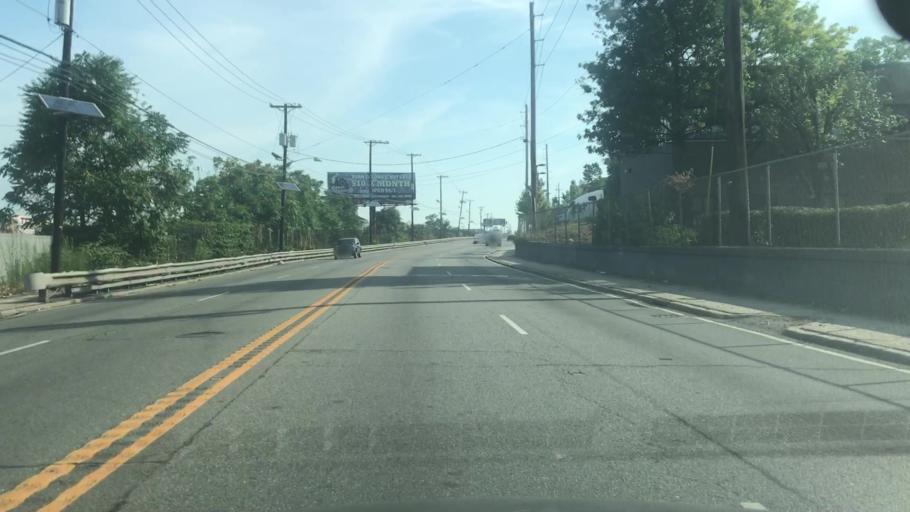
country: US
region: New Jersey
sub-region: Hudson County
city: West New York
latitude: 40.7961
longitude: -74.0256
